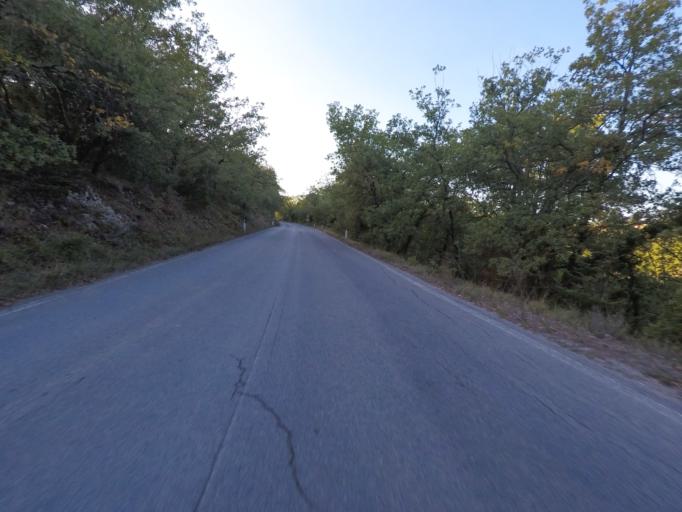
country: IT
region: Tuscany
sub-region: Provincia di Siena
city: Radda in Chianti
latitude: 43.4475
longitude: 11.3936
